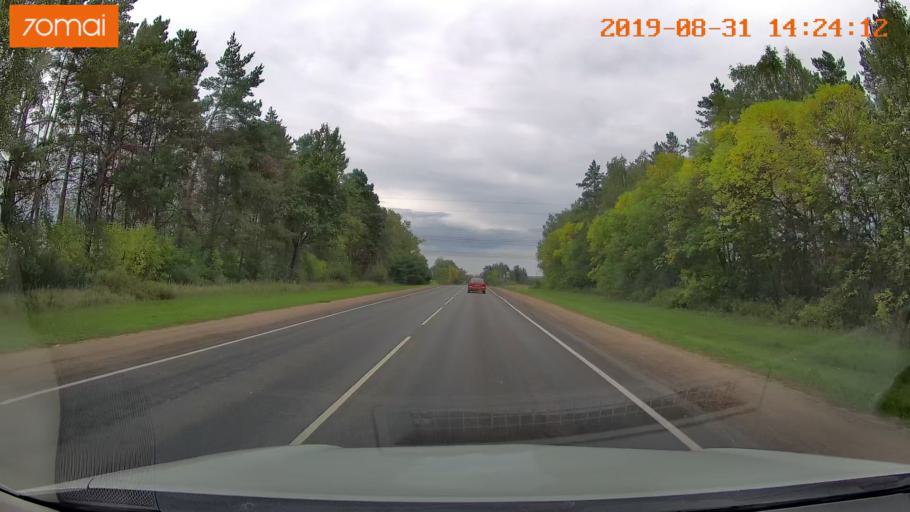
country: RU
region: Smolensk
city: Yekimovichi
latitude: 54.1015
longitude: 33.2506
